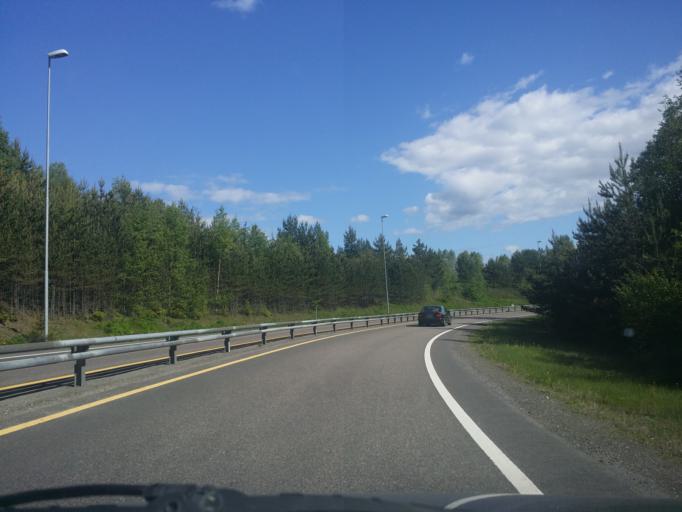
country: NO
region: Akershus
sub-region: Ullensaker
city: Jessheim
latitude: 60.1778
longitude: 11.0977
